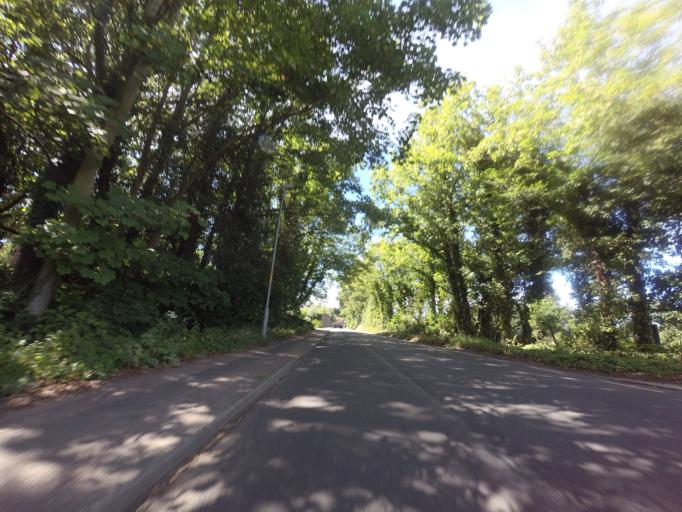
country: GB
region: England
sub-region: Kent
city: Sandwich
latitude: 51.2721
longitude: 1.3520
